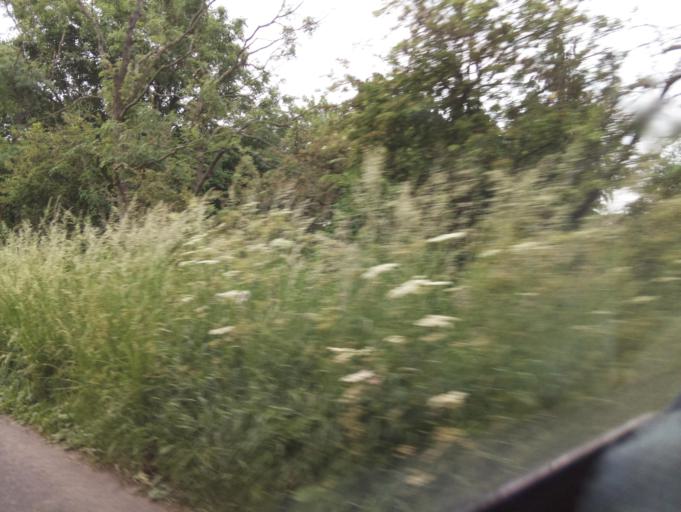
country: GB
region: England
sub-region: District of Rutland
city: Langham
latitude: 52.6824
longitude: -0.8257
